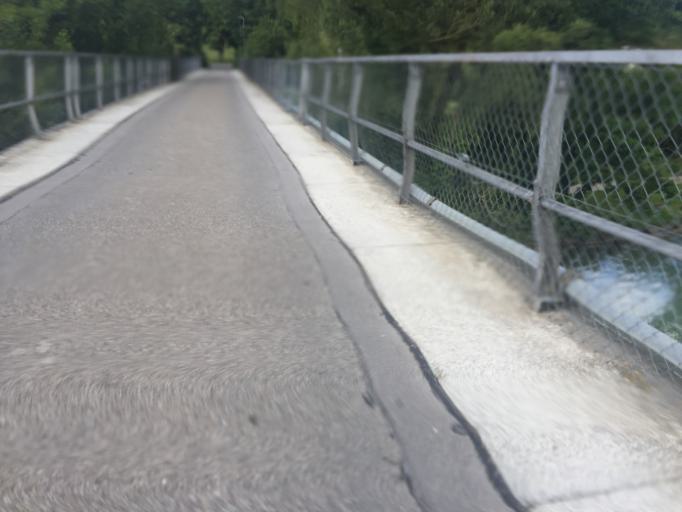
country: CH
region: Bern
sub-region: Bern-Mittelland District
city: Wohlen
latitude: 46.9665
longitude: 7.3589
